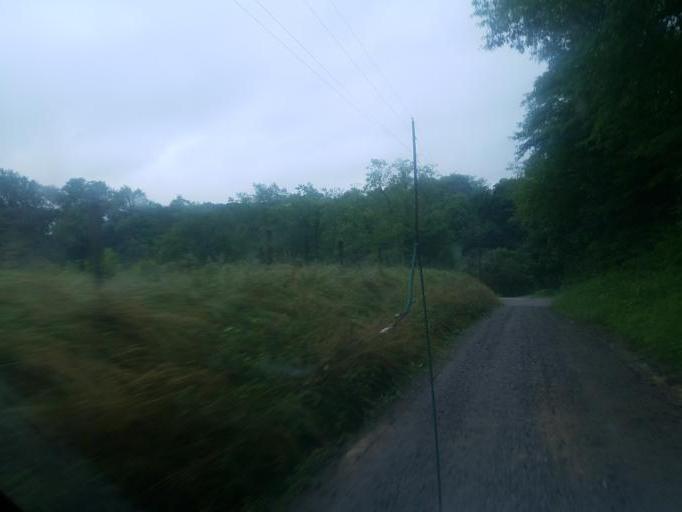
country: US
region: Ohio
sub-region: Columbiana County
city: Salineville
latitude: 40.6141
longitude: -80.8913
